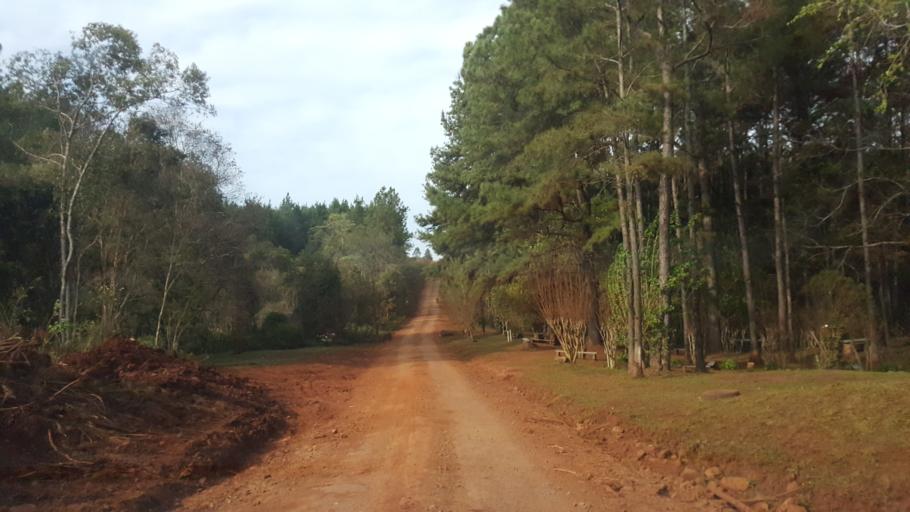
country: AR
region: Misiones
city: Capiovi
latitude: -26.9165
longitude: -55.1165
